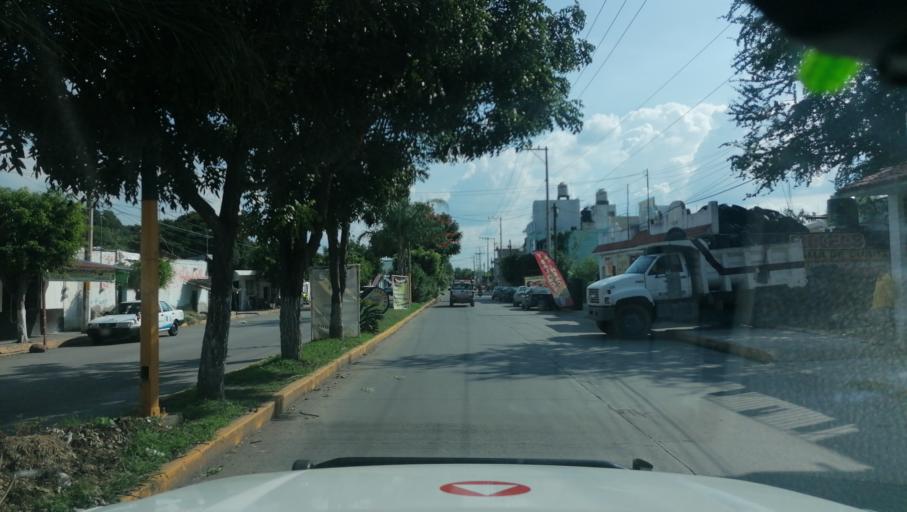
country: MX
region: Morelos
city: Cuautla Morelos
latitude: 18.8114
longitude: -98.9620
